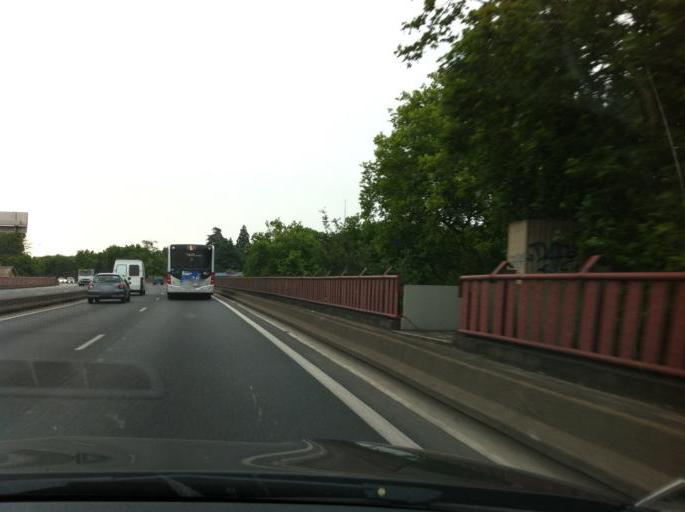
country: FR
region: Ile-de-France
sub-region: Departement de Seine-et-Marne
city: Melun
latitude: 48.5371
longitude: 2.6530
